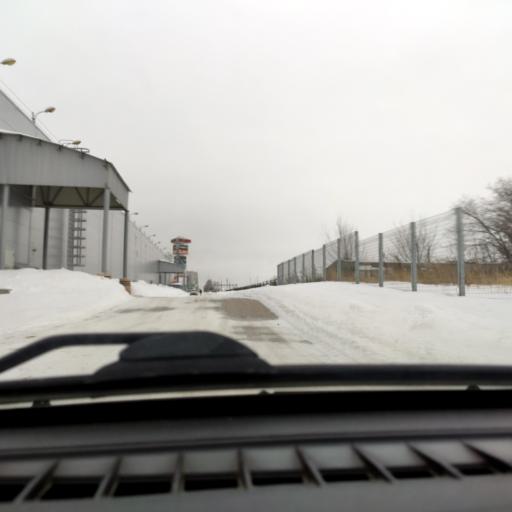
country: RU
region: Samara
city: Tol'yatti
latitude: 53.5439
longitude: 49.3873
